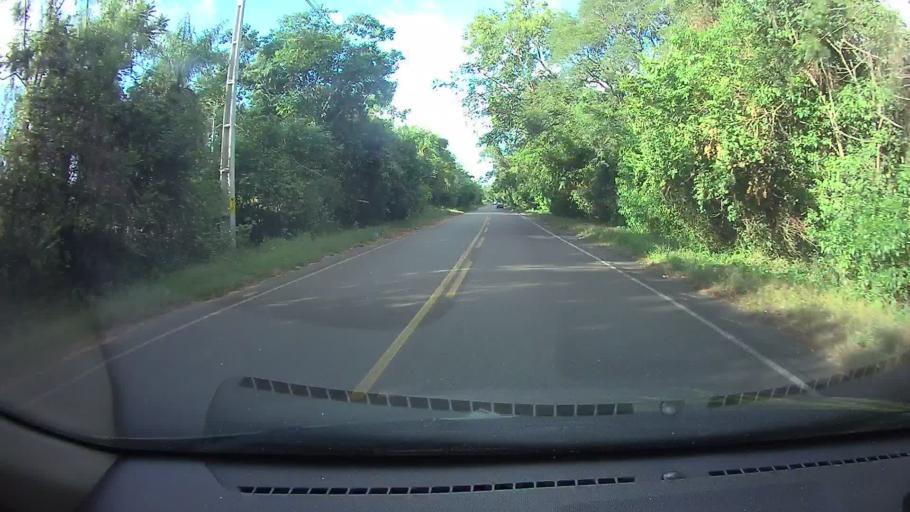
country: PY
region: Cordillera
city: Altos
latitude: -25.2272
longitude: -57.2268
